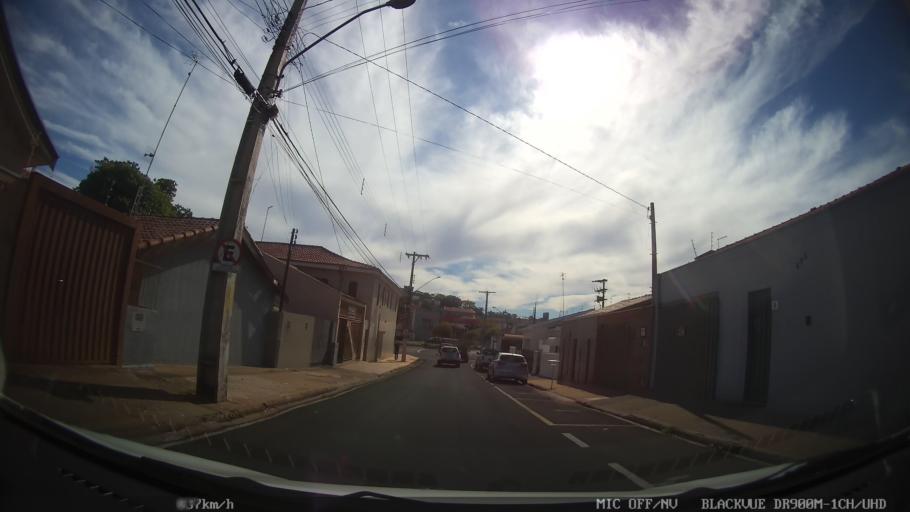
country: BR
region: Sao Paulo
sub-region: Catanduva
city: Catanduva
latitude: -21.1304
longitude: -48.9648
